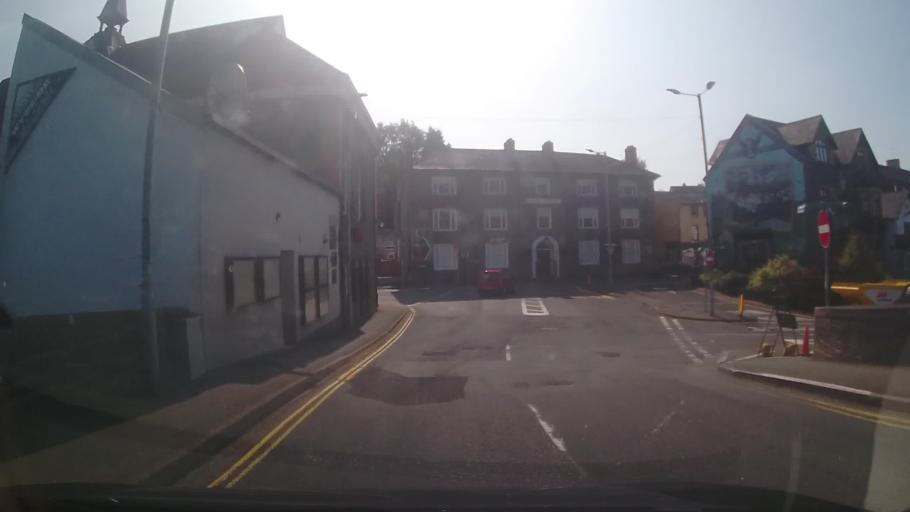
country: GB
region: Wales
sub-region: Sir Powys
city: Builth Wells
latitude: 52.1501
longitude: -3.4004
